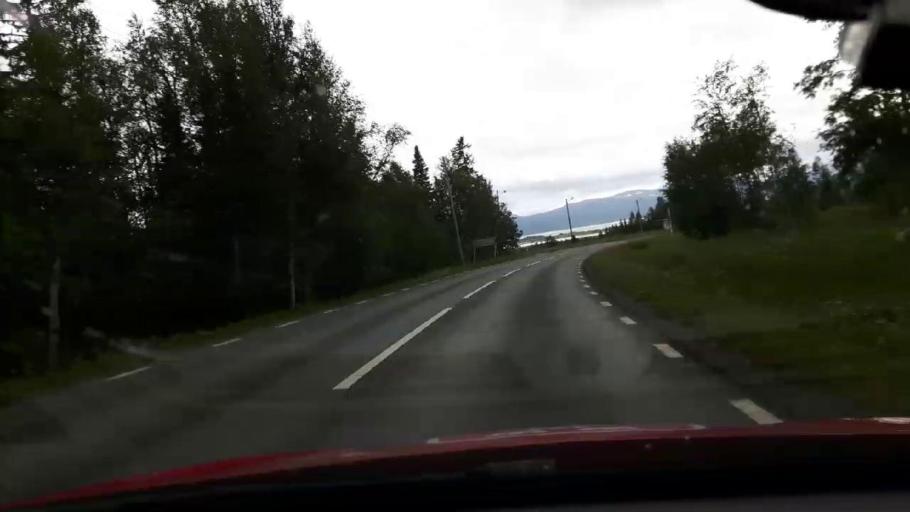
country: SE
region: Jaemtland
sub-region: Are Kommun
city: Are
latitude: 63.3275
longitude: 12.5569
